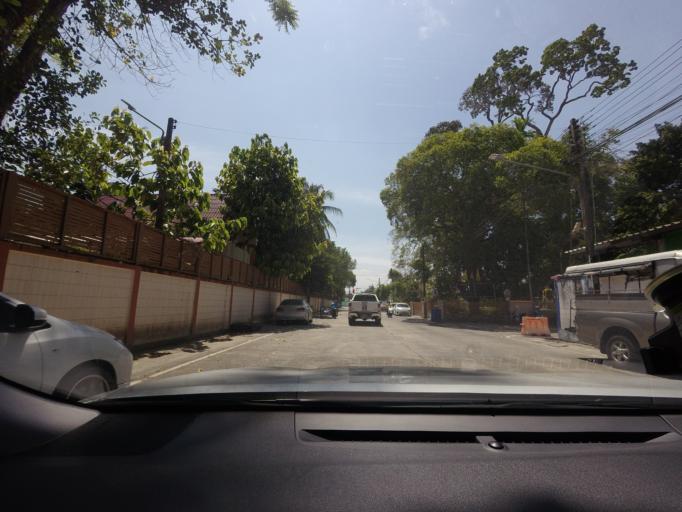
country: TH
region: Narathiwat
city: Narathiwat
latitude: 6.4249
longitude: 101.8212
